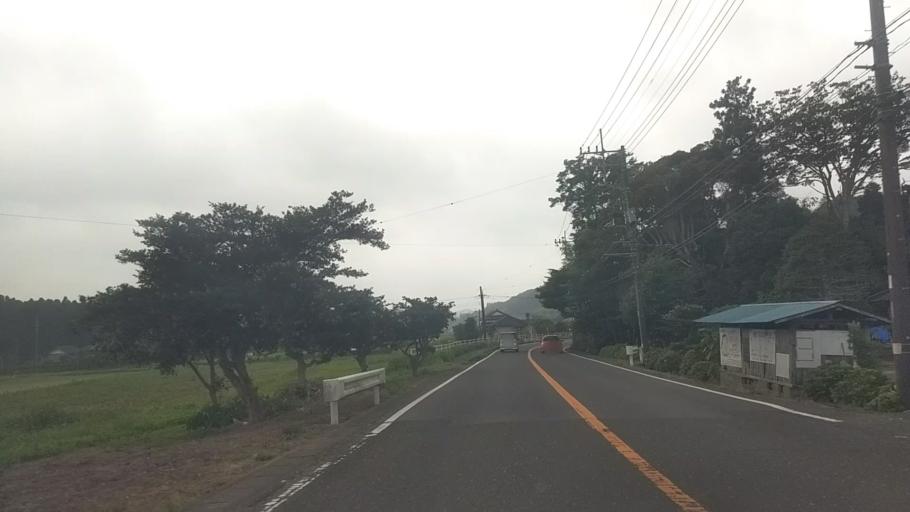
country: JP
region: Chiba
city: Ohara
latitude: 35.2799
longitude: 140.3257
